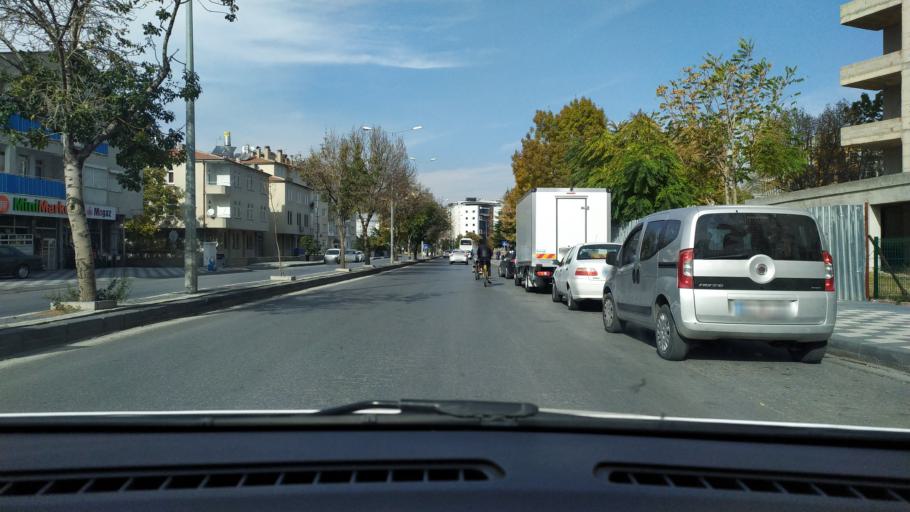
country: TR
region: Kayseri
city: Kayseri
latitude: 38.7094
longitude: 35.4916
